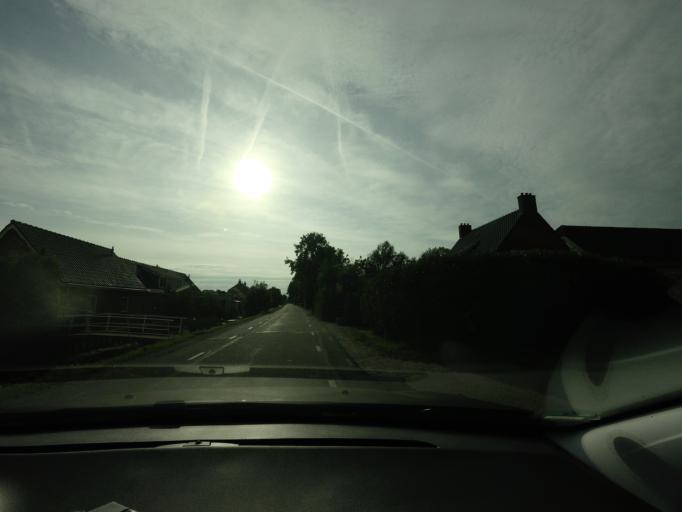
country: NL
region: Utrecht
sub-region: Gemeente Lopik
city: Lopik
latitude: 51.9830
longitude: 4.9884
